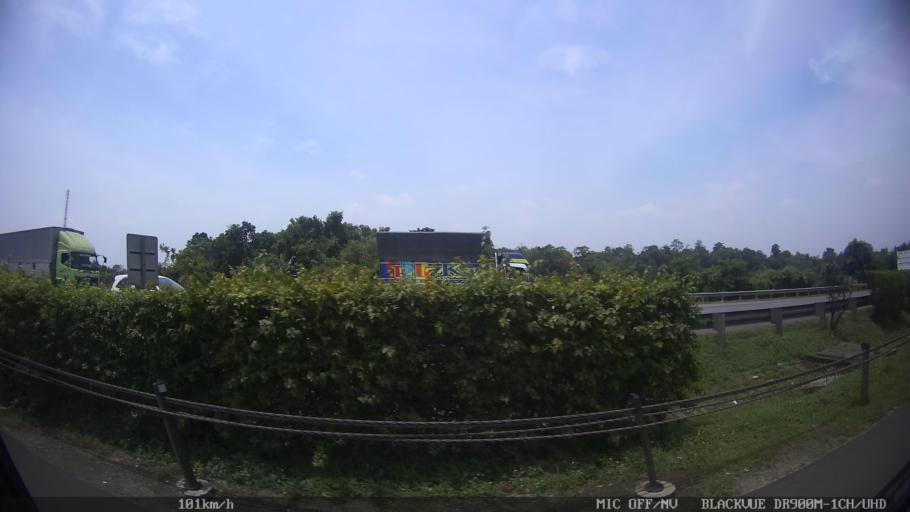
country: ID
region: West Java
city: Kresek
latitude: -6.1820
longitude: 106.3942
